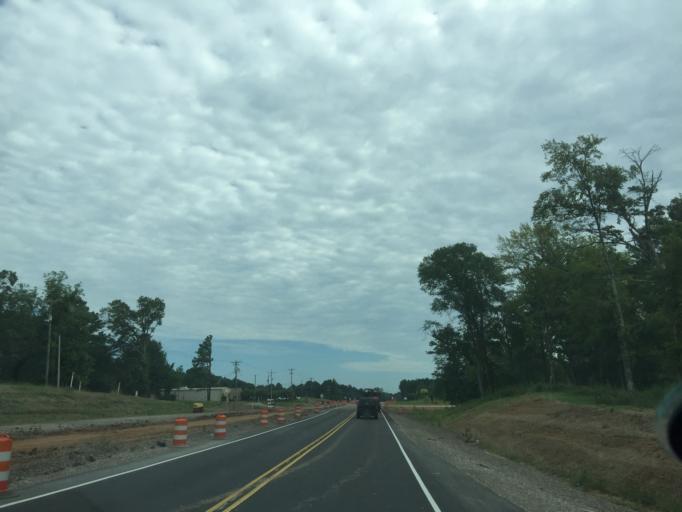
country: US
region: Mississippi
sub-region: Rankin County
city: Brandon
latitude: 32.2954
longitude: -89.9966
